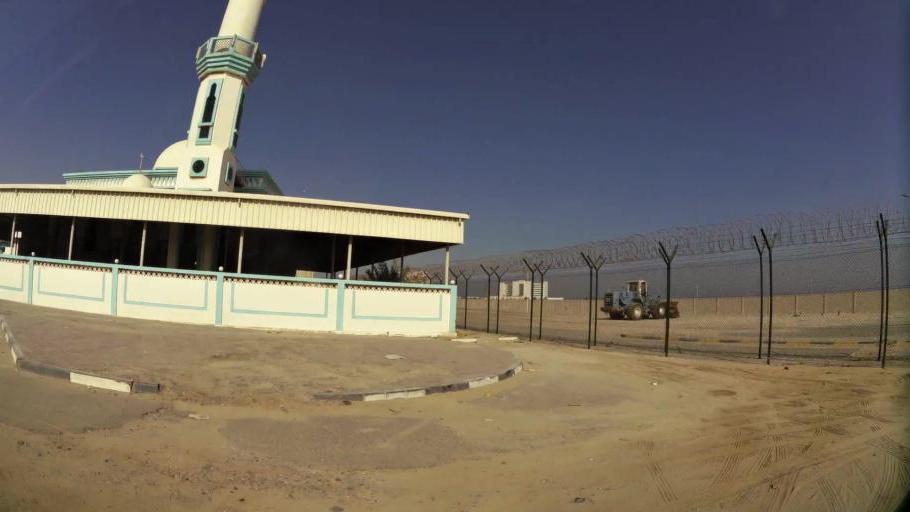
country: AE
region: Ajman
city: Ajman
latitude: 25.4222
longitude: 55.4505
